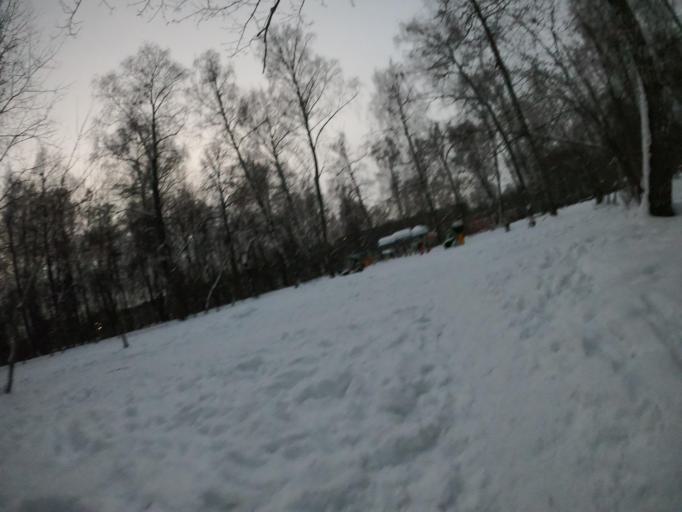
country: RU
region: Moskovskaya
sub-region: Podol'skiy Rayon
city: Podol'sk
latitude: 55.4176
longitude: 37.5249
